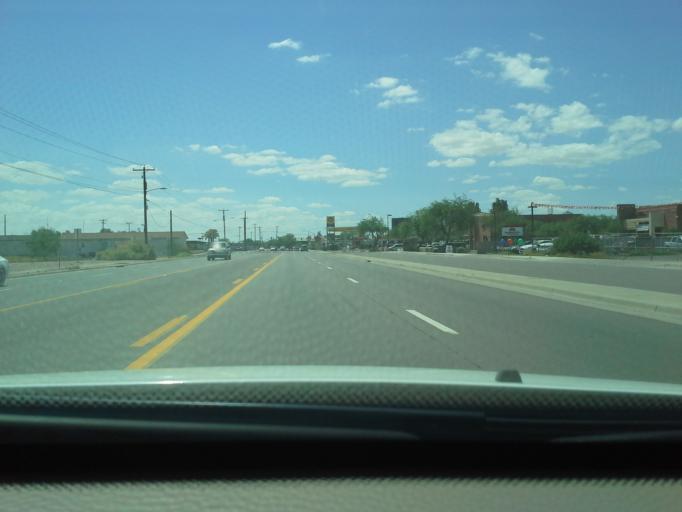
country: US
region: Arizona
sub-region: Pinal County
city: Maricopa
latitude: 33.0606
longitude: -112.0481
